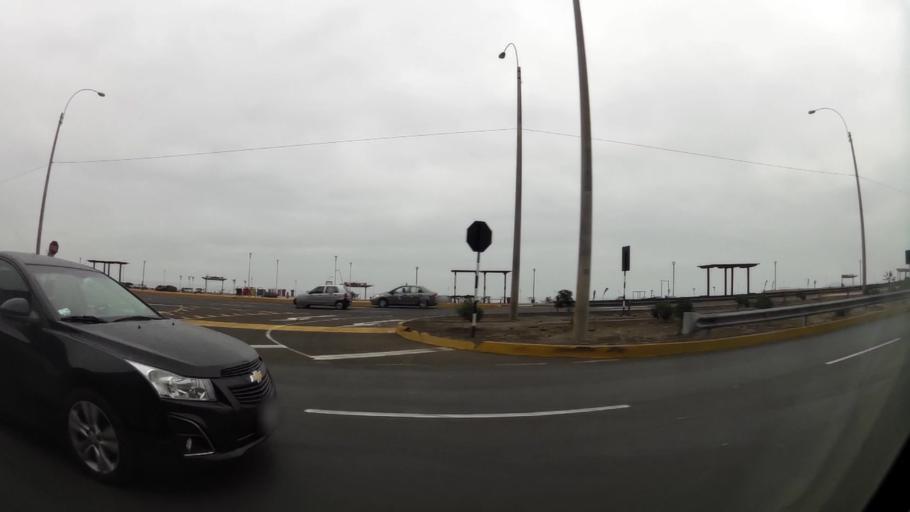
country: PE
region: Lima
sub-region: Lima
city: San Isidro
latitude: -12.0940
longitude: -77.0803
